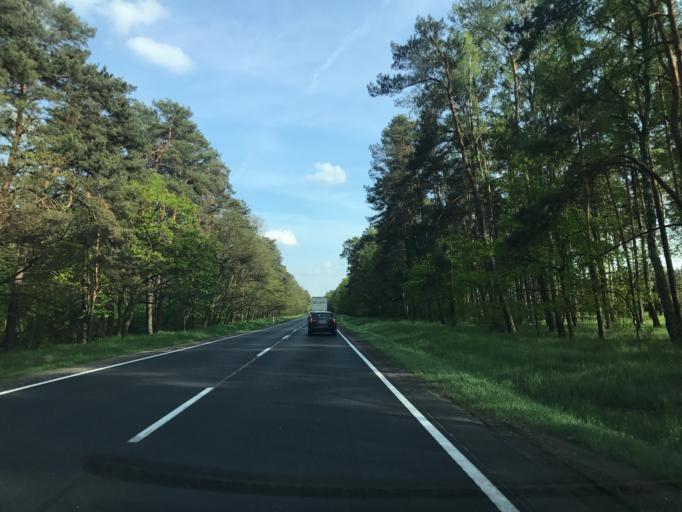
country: PL
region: Kujawsko-Pomorskie
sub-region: Powiat torunski
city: Wielka Nieszawka
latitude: 53.0274
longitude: 18.4167
